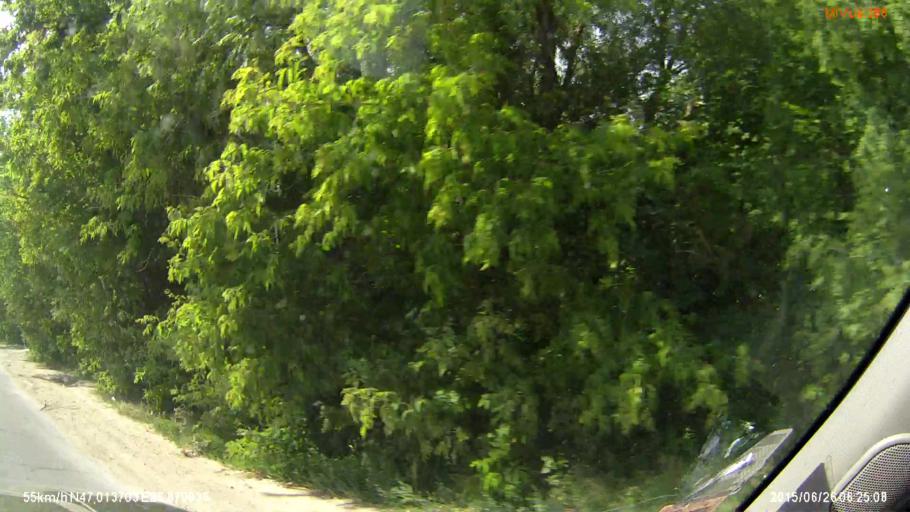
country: MD
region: Chisinau
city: Chisinau
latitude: 47.0138
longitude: 28.8708
